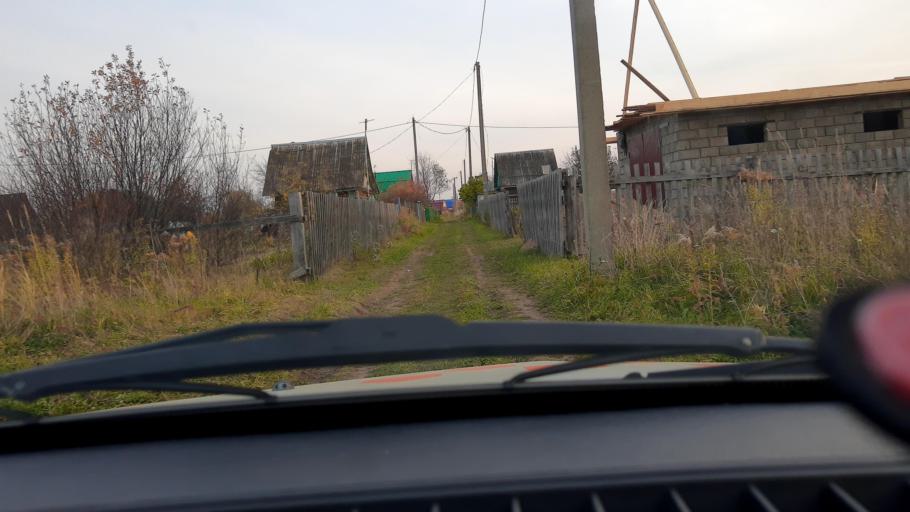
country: RU
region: Bashkortostan
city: Iglino
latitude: 54.8058
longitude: 56.3496
